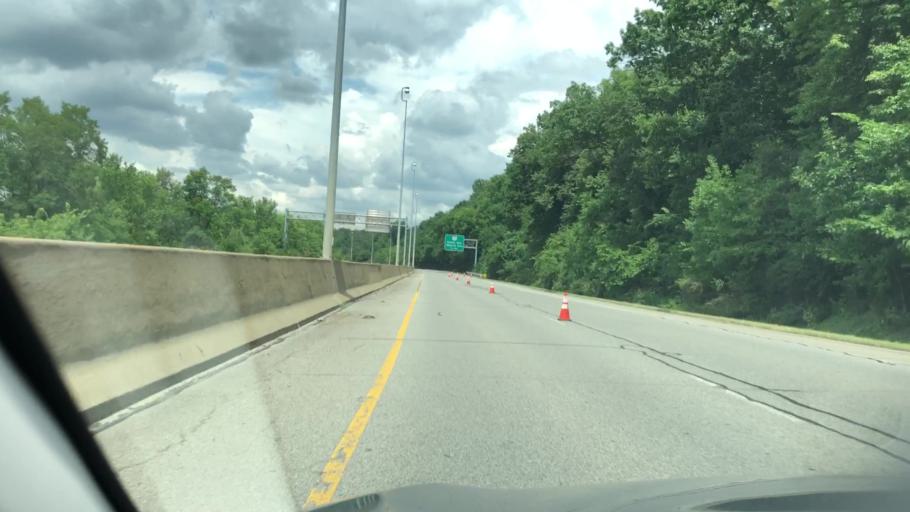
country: US
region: Ohio
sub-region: Stark County
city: Massillon
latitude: 40.7752
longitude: -81.5175
